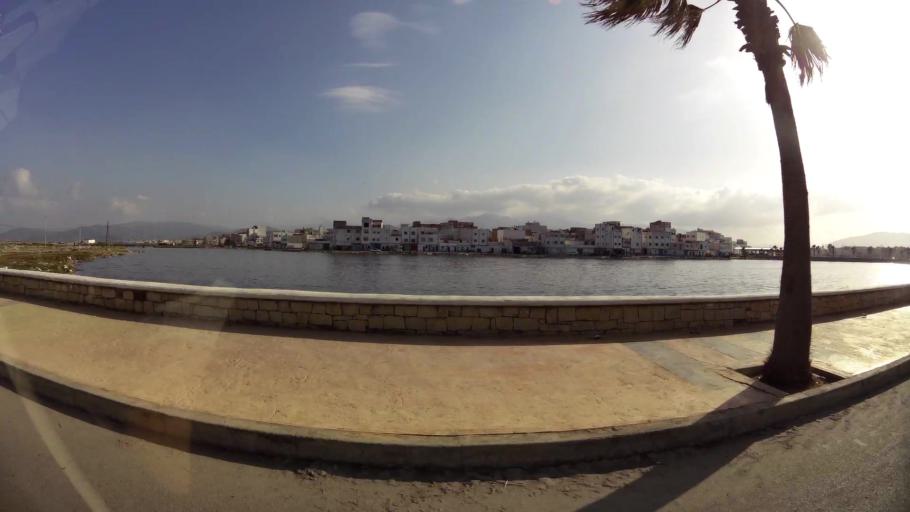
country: MA
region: Tanger-Tetouan
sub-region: Tetouan
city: Martil
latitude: 35.6147
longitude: -5.2711
